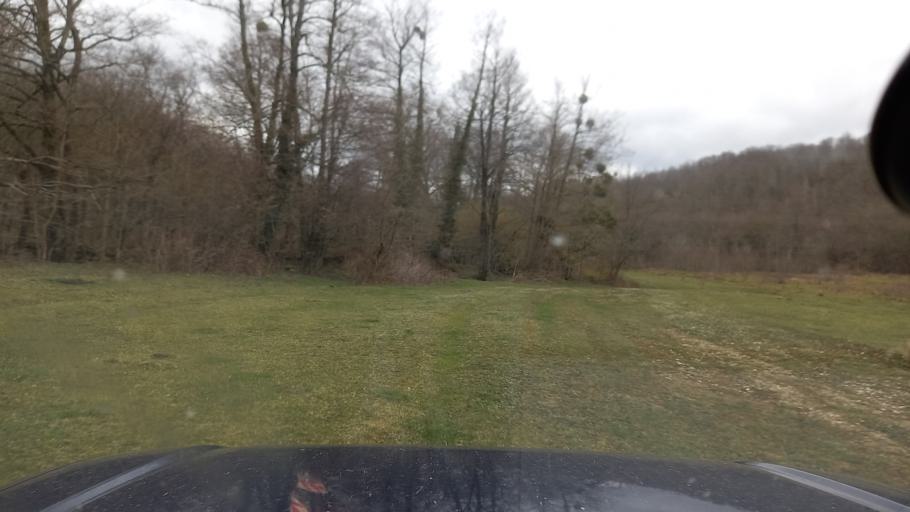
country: RU
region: Krasnodarskiy
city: Pshada
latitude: 44.4842
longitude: 38.4003
